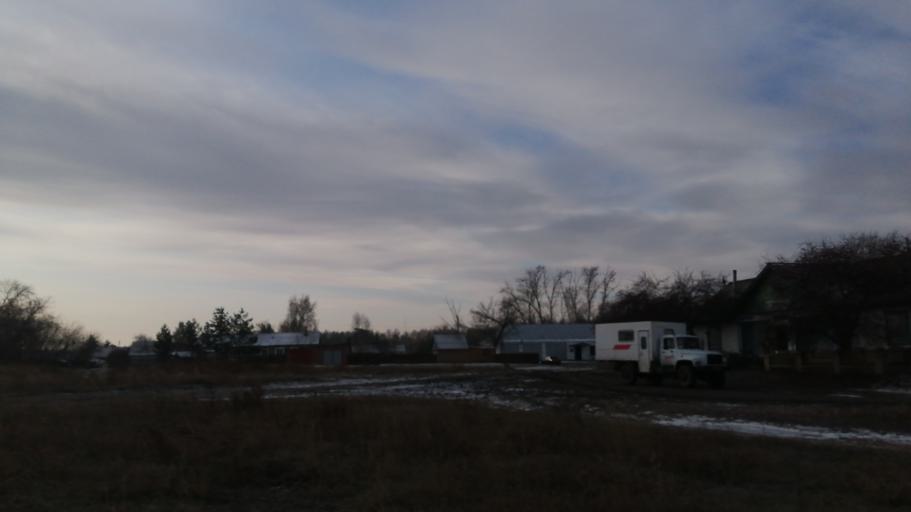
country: RU
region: Novosibirsk
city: Krasnozerskoye
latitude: 53.9888
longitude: 78.7241
